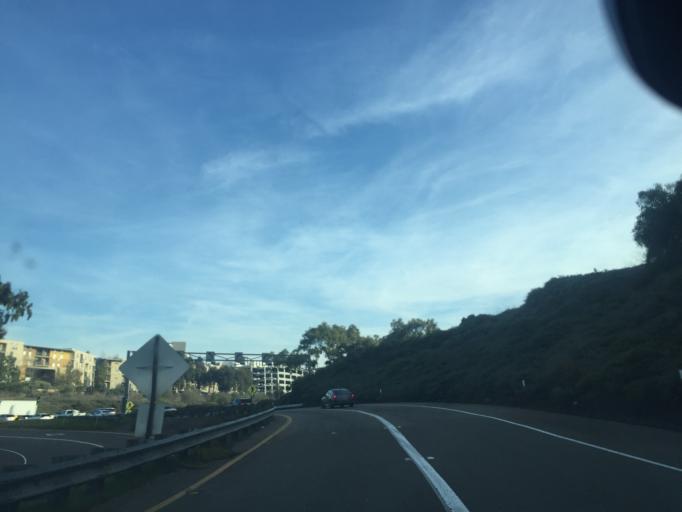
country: US
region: California
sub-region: San Diego County
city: La Jolla
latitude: 32.8712
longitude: -117.2281
